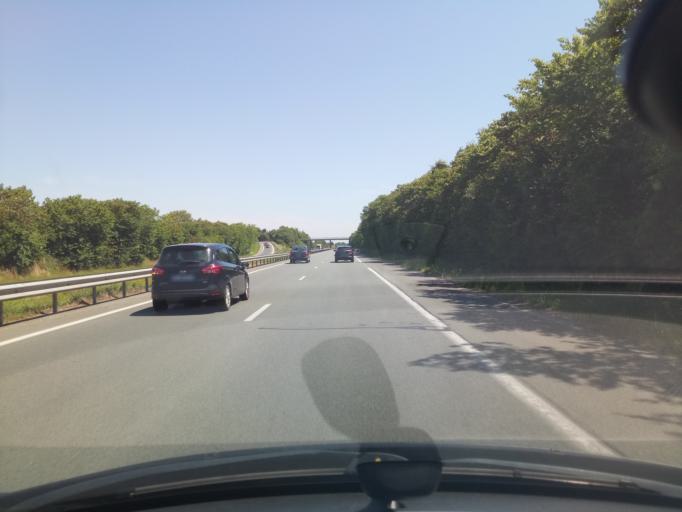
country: FR
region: Poitou-Charentes
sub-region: Departement de la Charente-Maritime
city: Dompierre-sur-Mer
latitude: 46.1873
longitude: -1.0744
